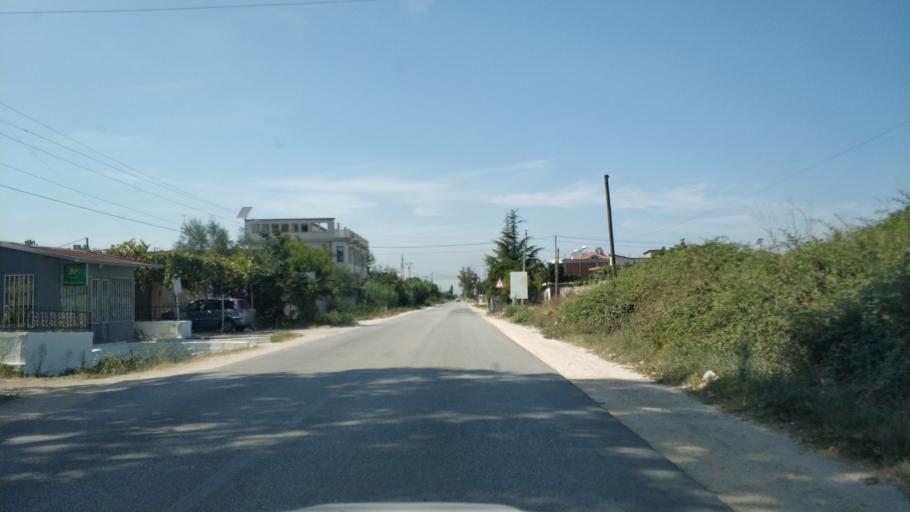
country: AL
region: Fier
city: Fier
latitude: 40.7294
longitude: 19.5446
